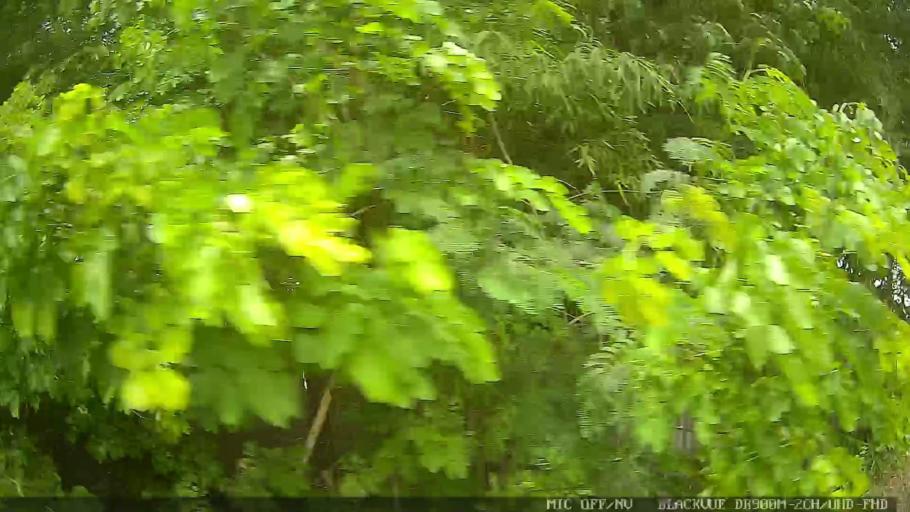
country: BR
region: Sao Paulo
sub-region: Conchas
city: Conchas
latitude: -23.0931
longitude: -47.9844
